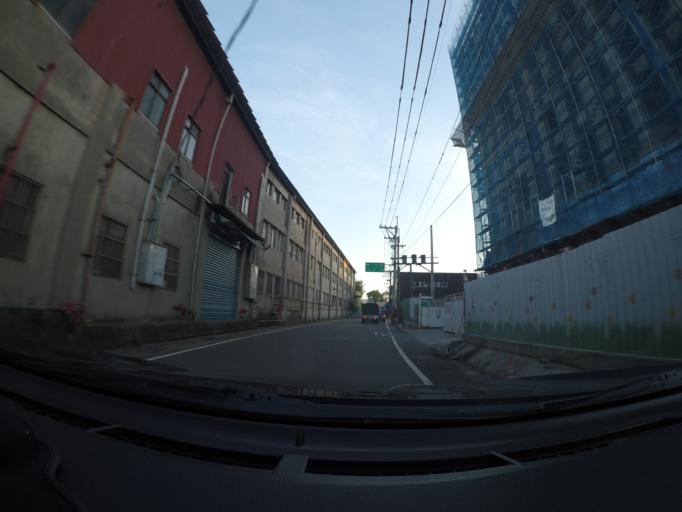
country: TW
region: Taiwan
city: Taoyuan City
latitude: 24.9939
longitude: 121.2738
